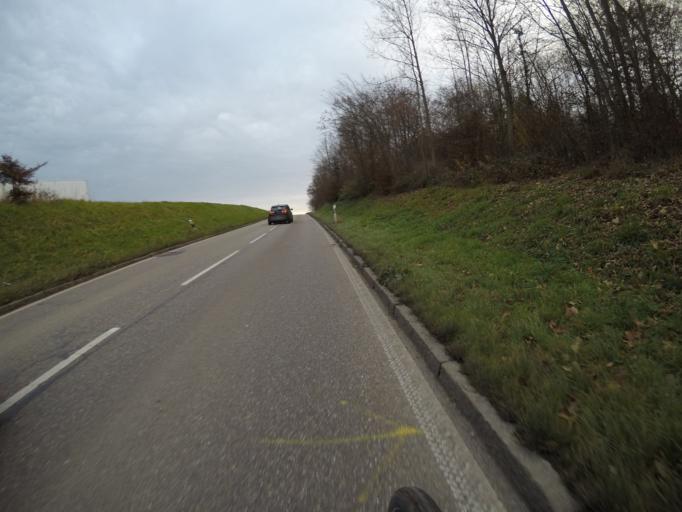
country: DE
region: Baden-Wuerttemberg
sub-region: Regierungsbezirk Stuttgart
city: Ostfildern
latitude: 48.7087
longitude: 9.2409
